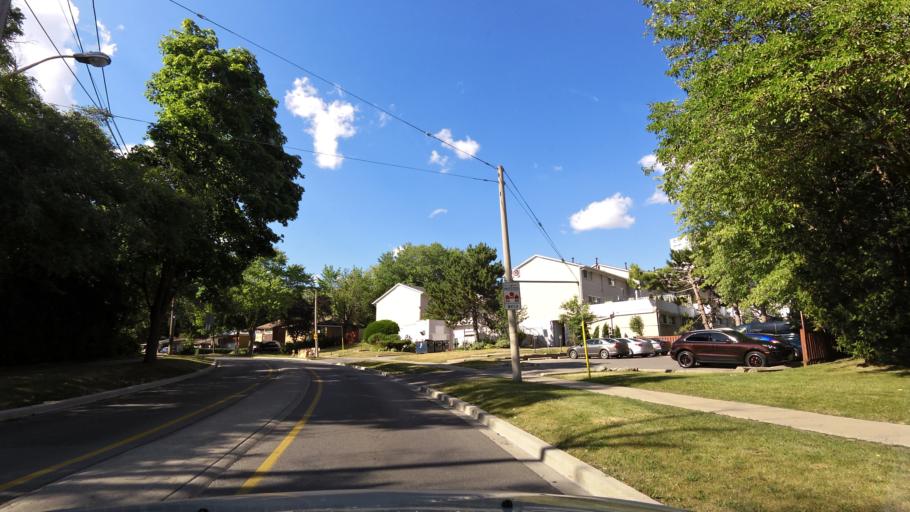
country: CA
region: Ontario
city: Willowdale
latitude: 43.7769
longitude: -79.3529
